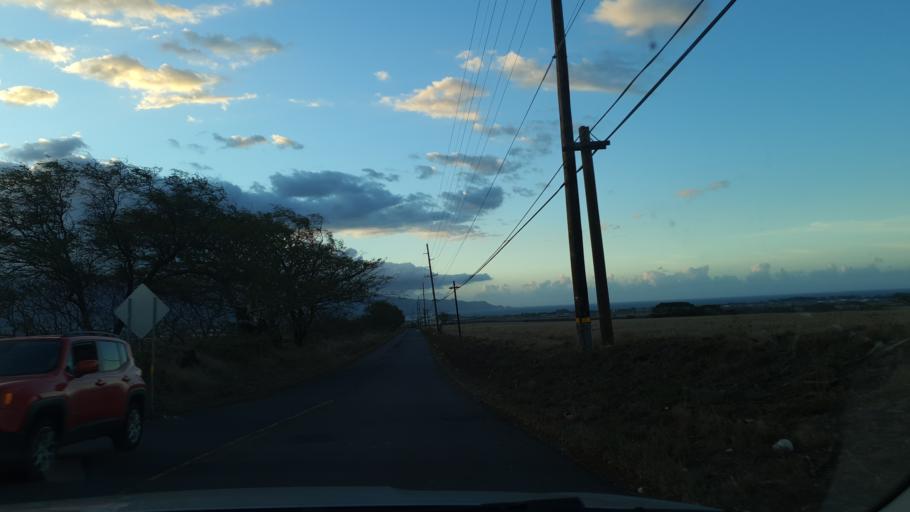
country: US
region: Hawaii
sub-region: Maui County
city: Kahului
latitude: 20.8607
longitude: -156.4268
